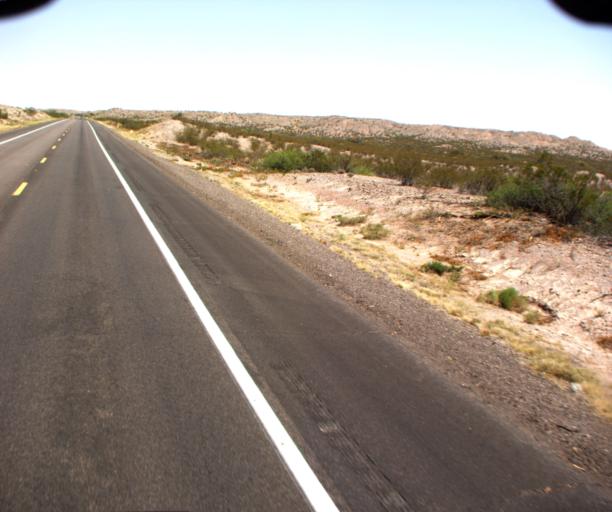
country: US
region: New Mexico
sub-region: Hidalgo County
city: Lordsburg
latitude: 32.6523
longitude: -109.0570
